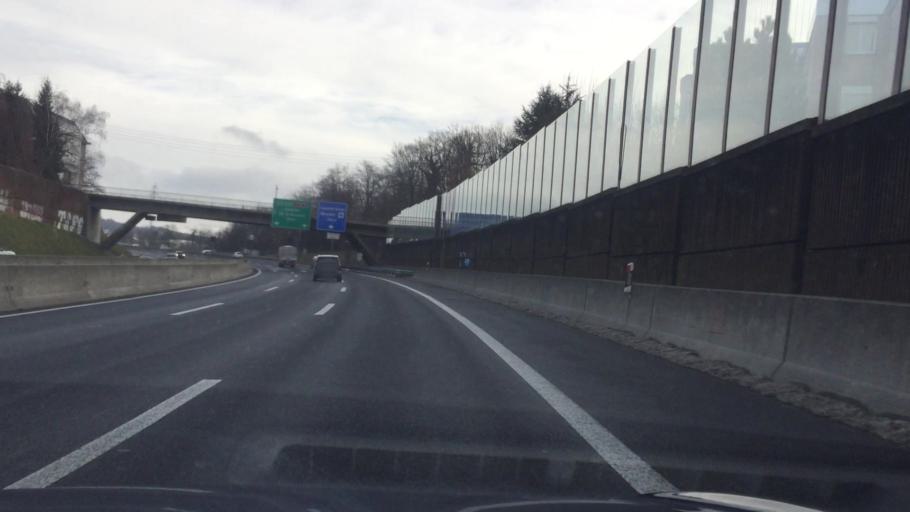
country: CH
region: Vaud
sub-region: Lausanne District
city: Blecherette
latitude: 46.5425
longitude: 6.6366
